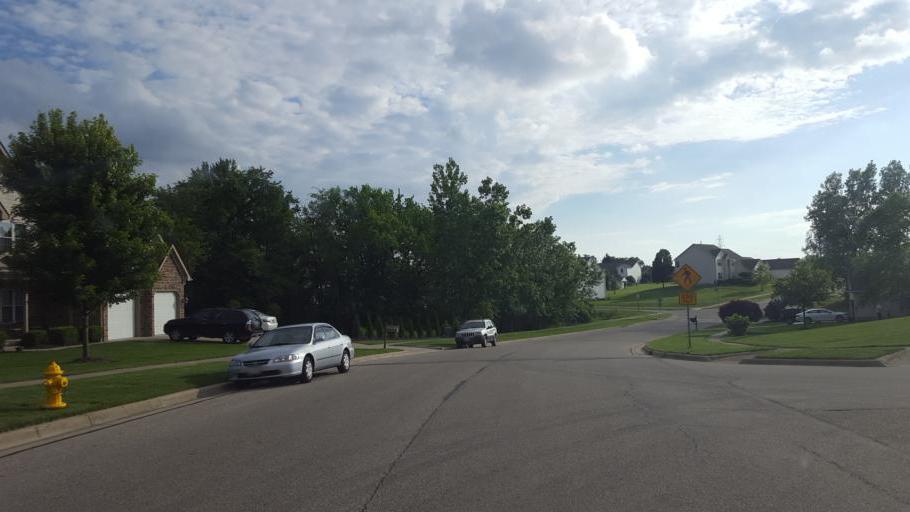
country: US
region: Ohio
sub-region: Delaware County
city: Lewis Center
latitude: 40.1772
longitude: -82.9878
